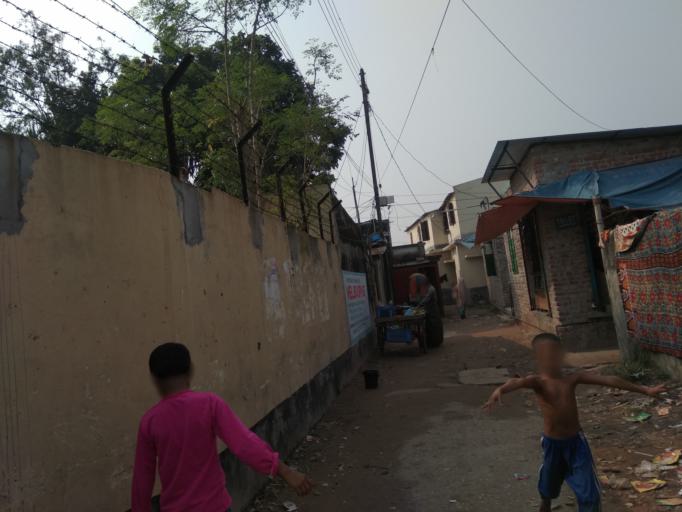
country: BD
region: Dhaka
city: Tungi
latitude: 23.8593
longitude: 90.3861
